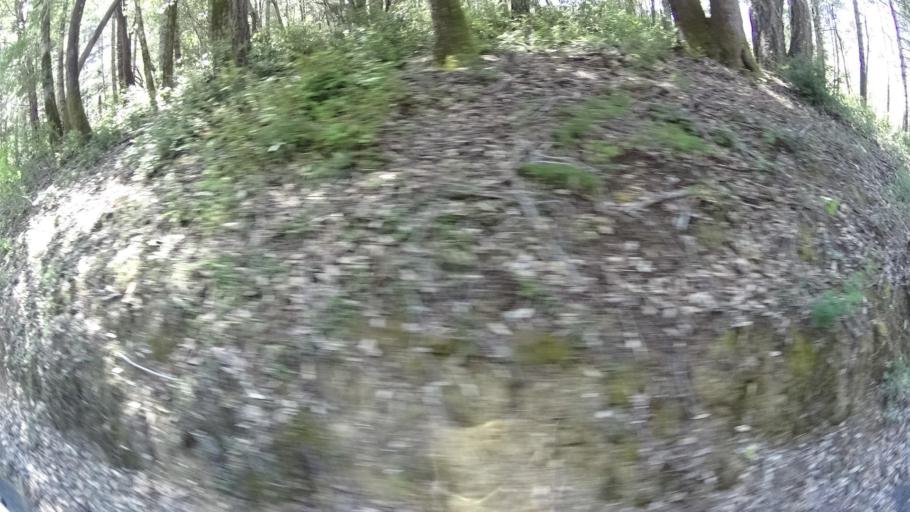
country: US
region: California
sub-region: Humboldt County
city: Rio Dell
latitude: 40.3270
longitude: -124.0460
